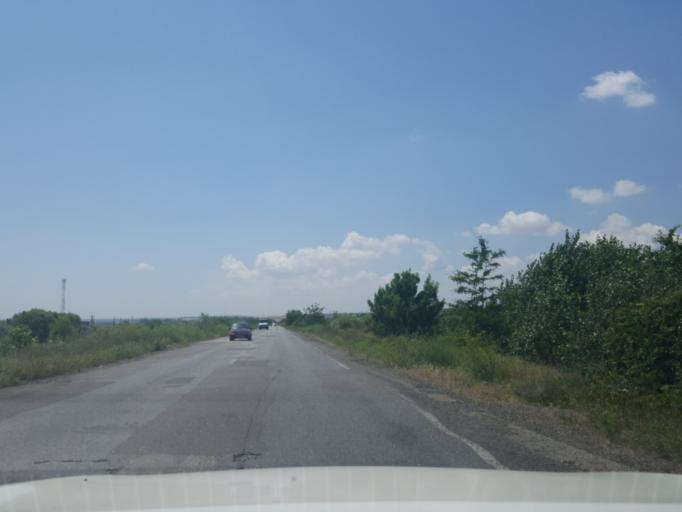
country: UA
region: Odessa
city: Bilyayivka
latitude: 46.4070
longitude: 30.1060
